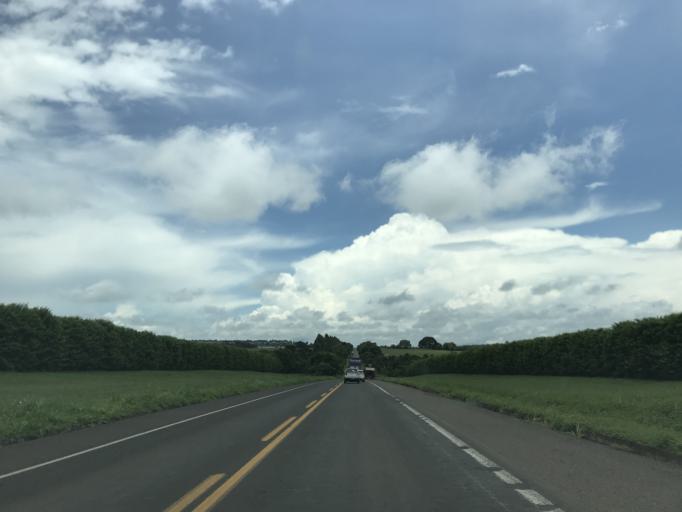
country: BR
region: Minas Gerais
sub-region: Frutal
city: Frutal
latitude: -19.7029
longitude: -48.9817
